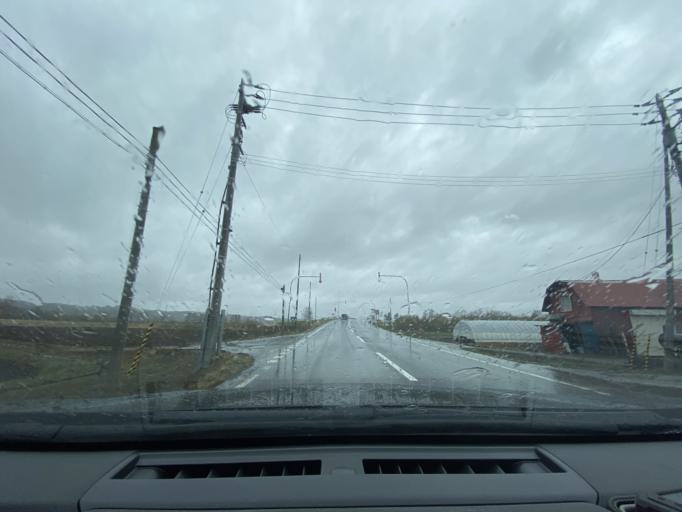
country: JP
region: Hokkaido
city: Fukagawa
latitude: 43.8090
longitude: 142.0174
